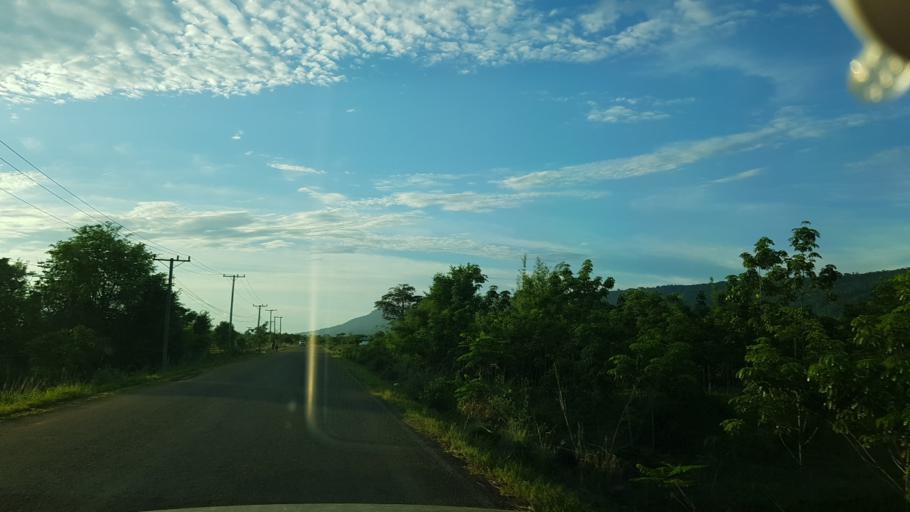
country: TH
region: Nong Khai
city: Sangkhom
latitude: 18.1106
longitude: 102.2915
